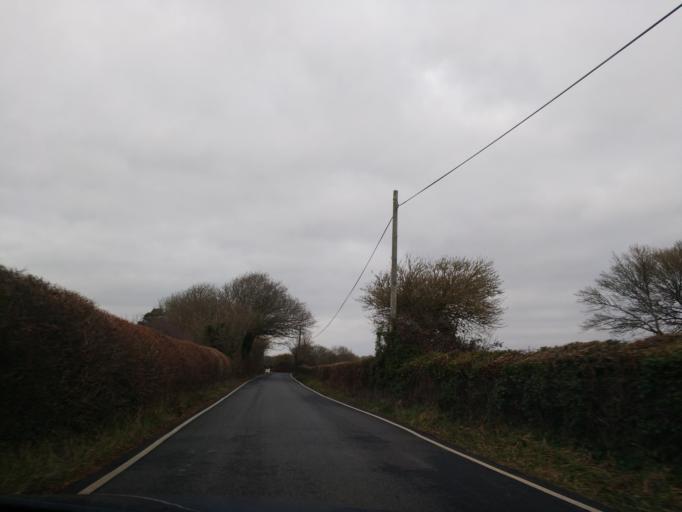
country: GB
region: England
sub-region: Isle of Wight
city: Shalfleet
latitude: 50.7031
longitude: -1.4093
